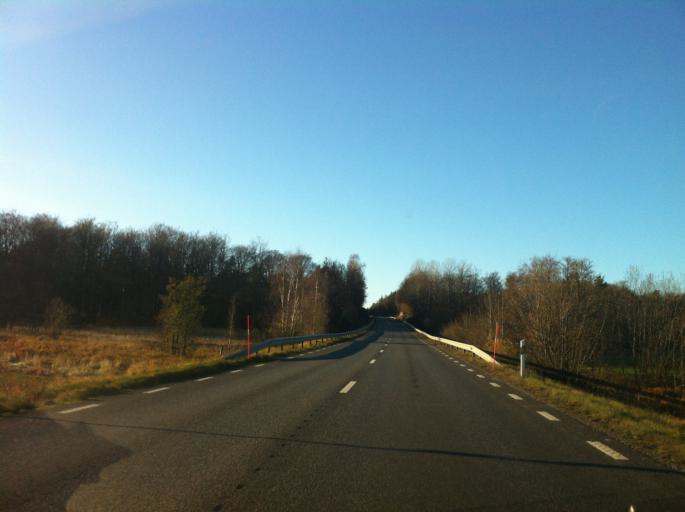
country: SE
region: Blekinge
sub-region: Karlshamns Kommun
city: Morrum
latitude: 56.1686
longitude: 14.6722
